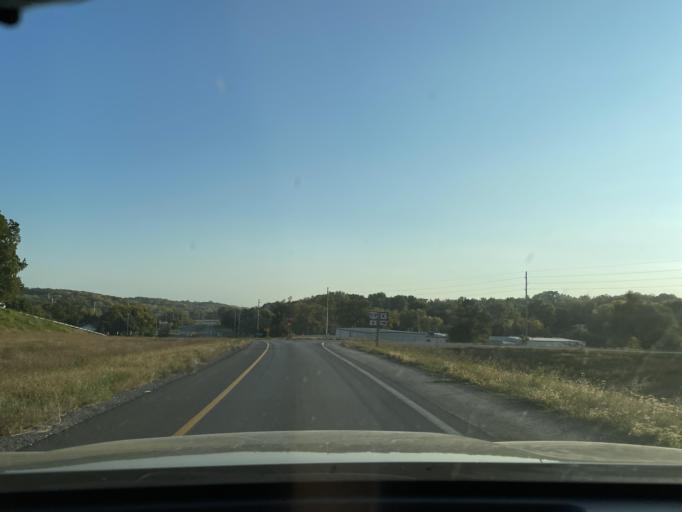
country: US
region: Missouri
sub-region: Andrew County
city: Country Club Village
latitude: 39.8160
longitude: -94.8405
